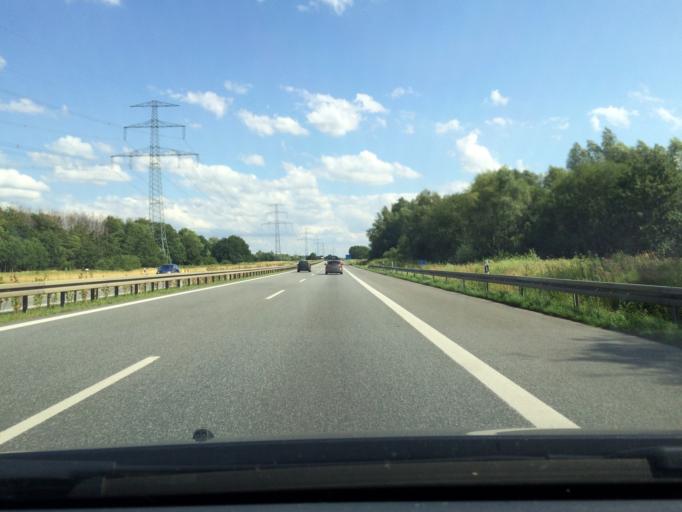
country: DE
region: Mecklenburg-Vorpommern
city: Dierkow-West
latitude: 54.1348
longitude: 12.1368
